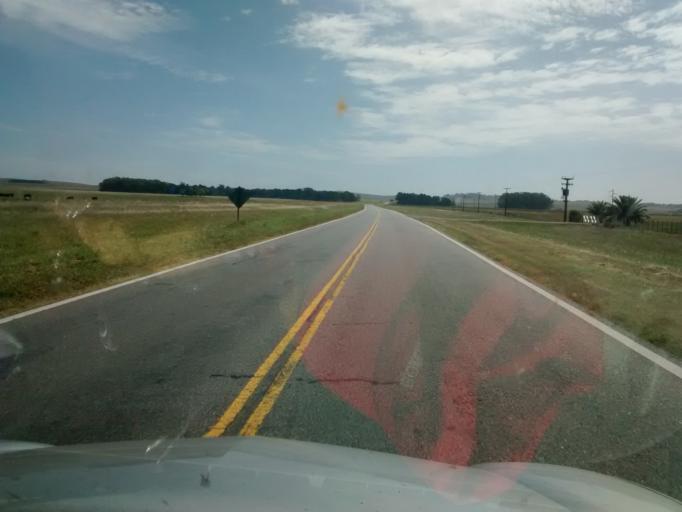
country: AR
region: Buenos Aires
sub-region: Partido de Balcarce
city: Balcarce
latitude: -37.6588
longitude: -58.5575
